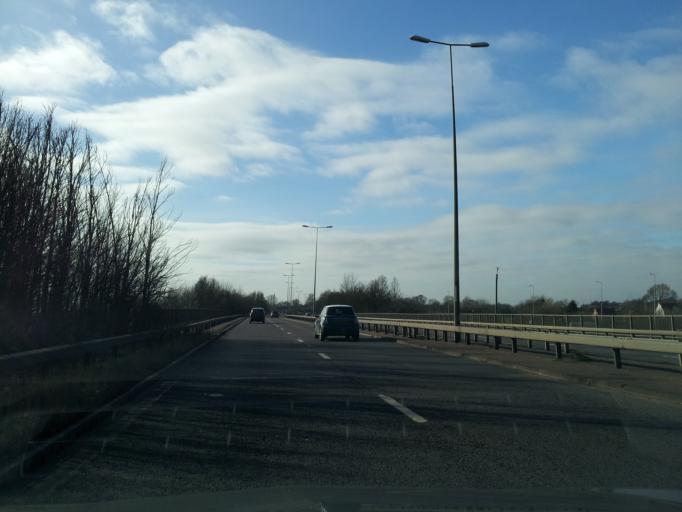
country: GB
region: England
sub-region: Derbyshire
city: Long Eaton
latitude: 52.9162
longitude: -1.2984
